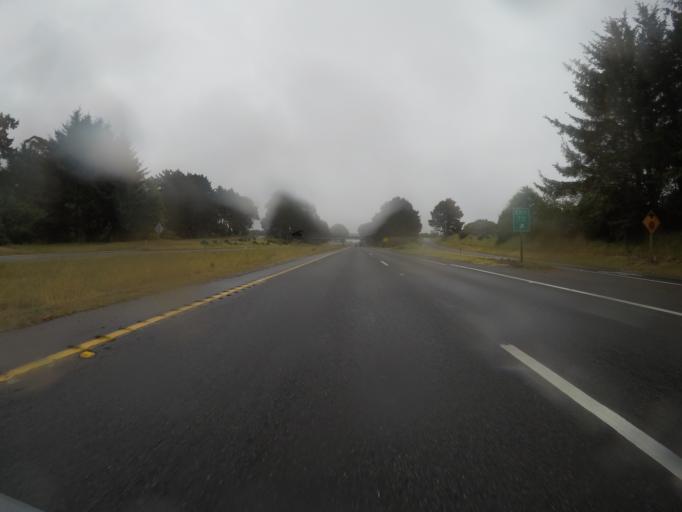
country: US
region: California
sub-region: Humboldt County
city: McKinleyville
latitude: 40.9581
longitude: -124.1162
